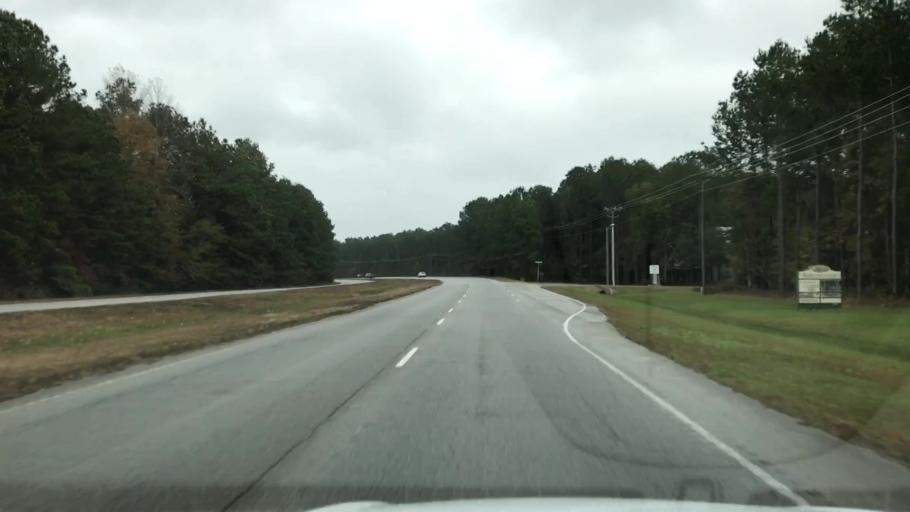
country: US
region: South Carolina
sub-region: Charleston County
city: Awendaw
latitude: 32.9460
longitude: -79.7019
